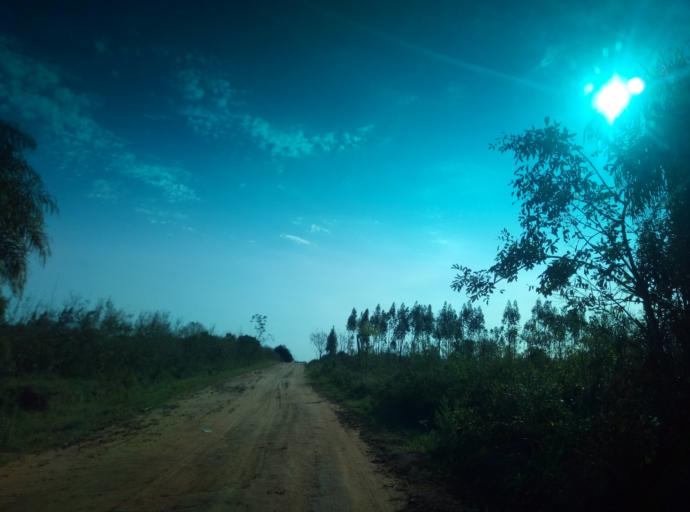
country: PY
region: Caaguazu
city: Doctor Cecilio Baez
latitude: -25.1648
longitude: -56.2289
